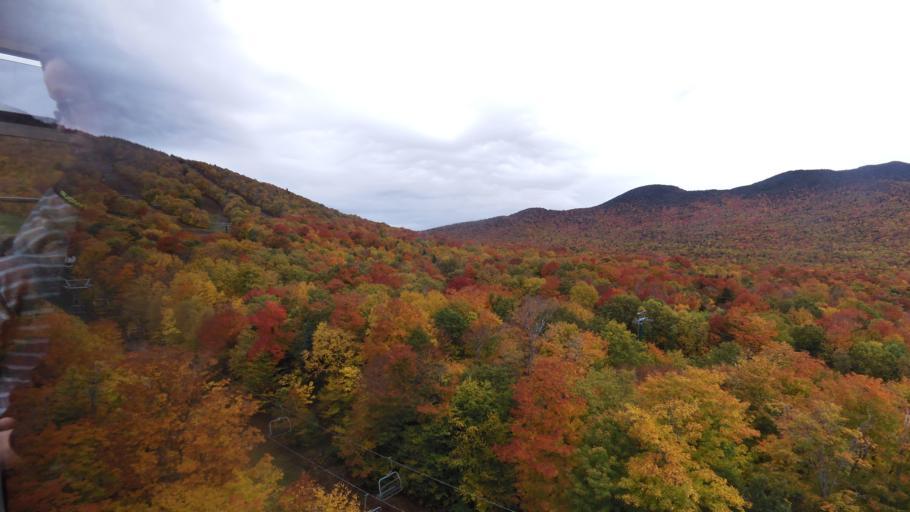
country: US
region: Vermont
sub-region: Franklin County
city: Richford
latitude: 44.9356
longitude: -72.5113
